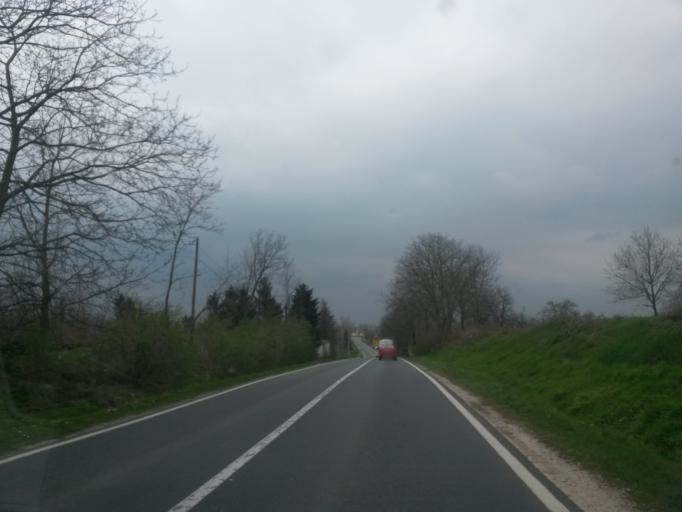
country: HR
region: Vukovarsko-Srijemska
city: Slakovci
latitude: 45.2128
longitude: 18.9915
